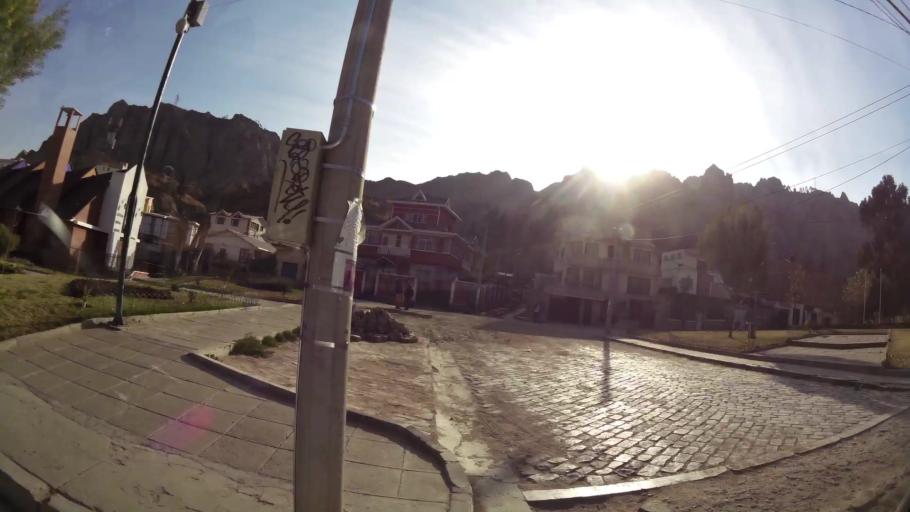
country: BO
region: La Paz
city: La Paz
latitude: -16.5203
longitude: -68.0903
